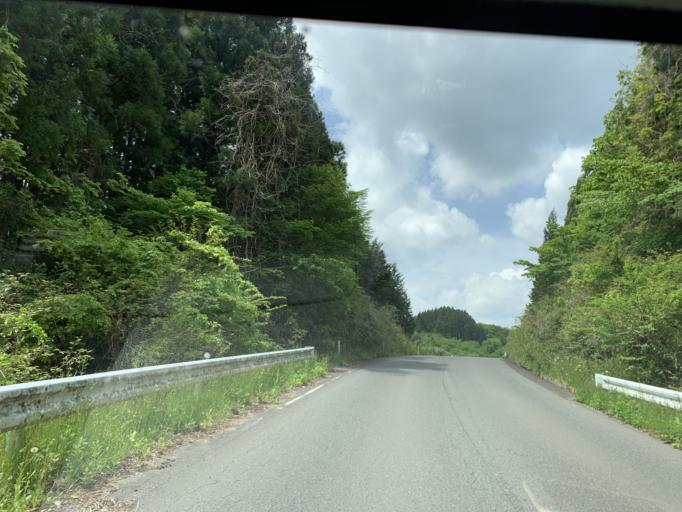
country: JP
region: Miyagi
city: Furukawa
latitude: 38.7204
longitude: 140.9221
